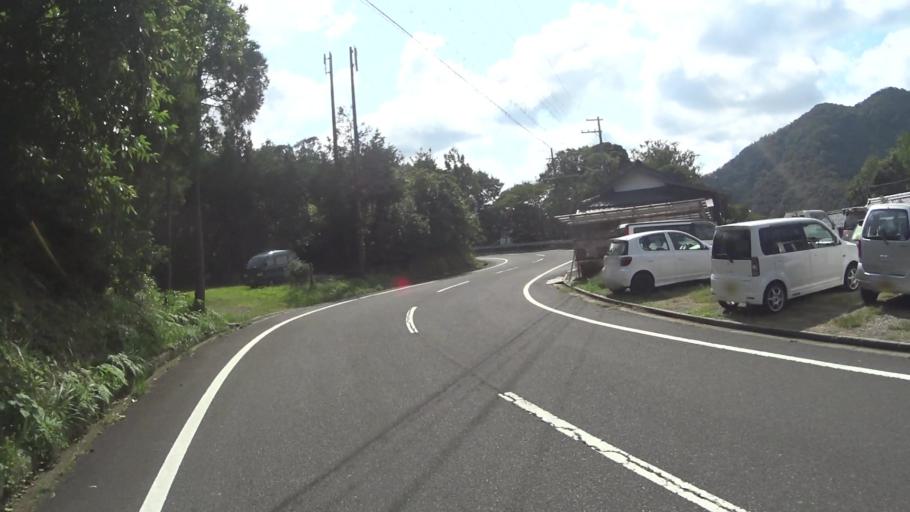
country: JP
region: Kyoto
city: Miyazu
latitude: 35.7508
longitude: 135.1676
